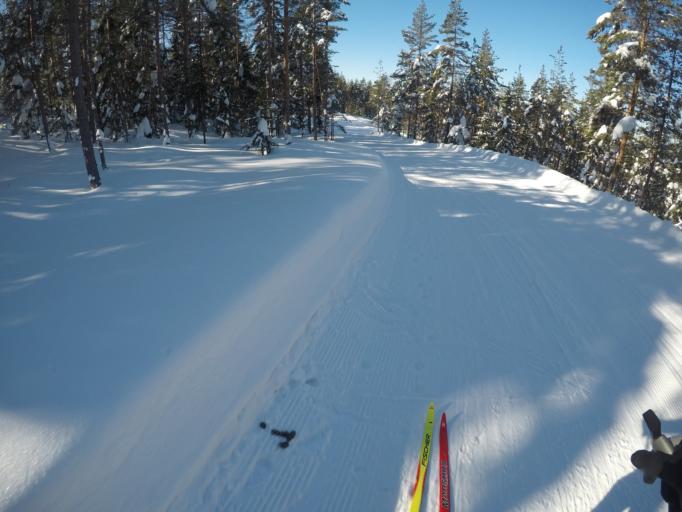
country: SE
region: Vaesternorrland
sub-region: Sundsvalls Kommun
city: Sundsvall
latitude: 62.3669
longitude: 17.3003
